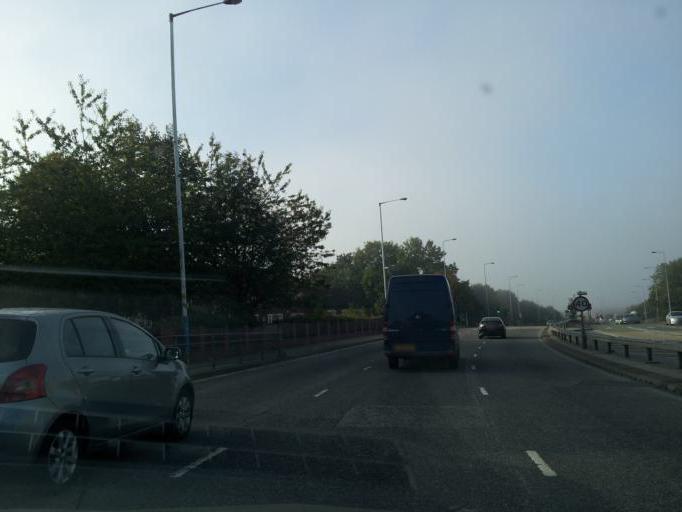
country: GB
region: England
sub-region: Manchester
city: Failsworth
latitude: 53.5315
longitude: -2.1534
